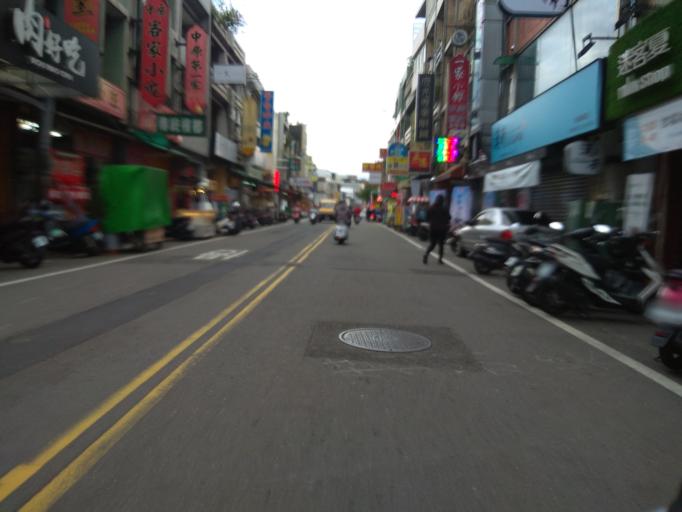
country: TW
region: Taiwan
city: Daxi
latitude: 24.8651
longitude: 121.2139
